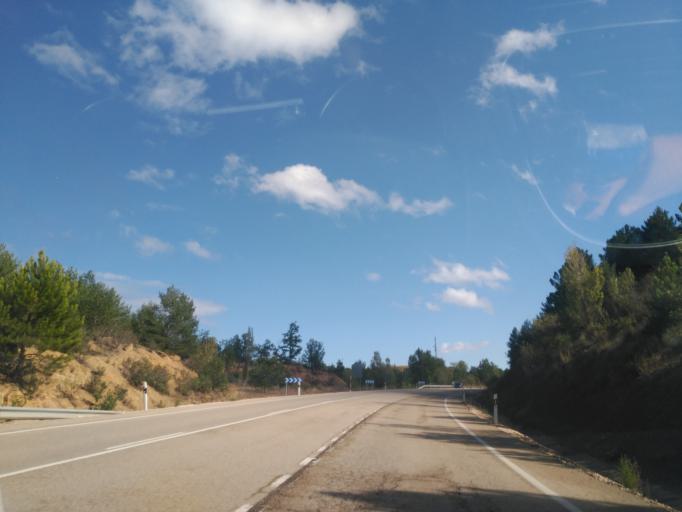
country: ES
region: Castille and Leon
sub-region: Provincia de Burgos
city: Pinilla de los Barruecos
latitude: 41.9030
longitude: -3.2731
